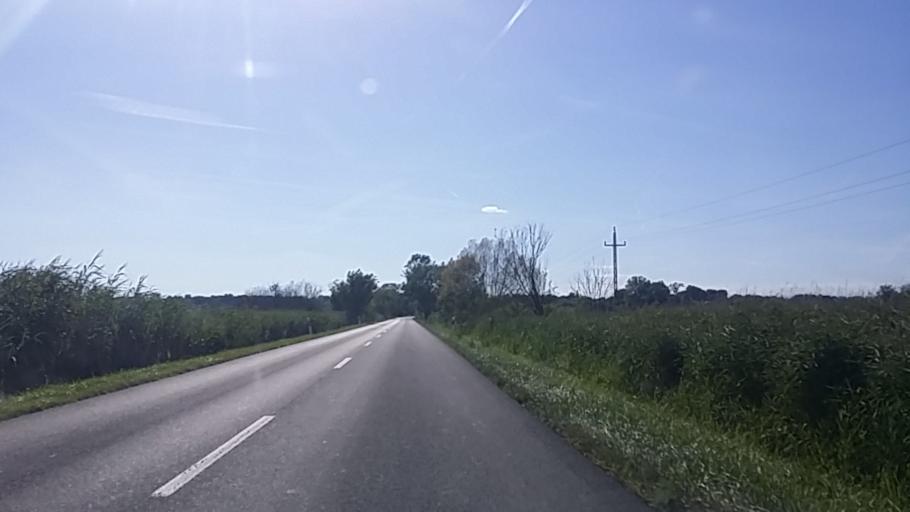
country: HU
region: Zala
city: Sarmellek
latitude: 46.7074
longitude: 17.1820
